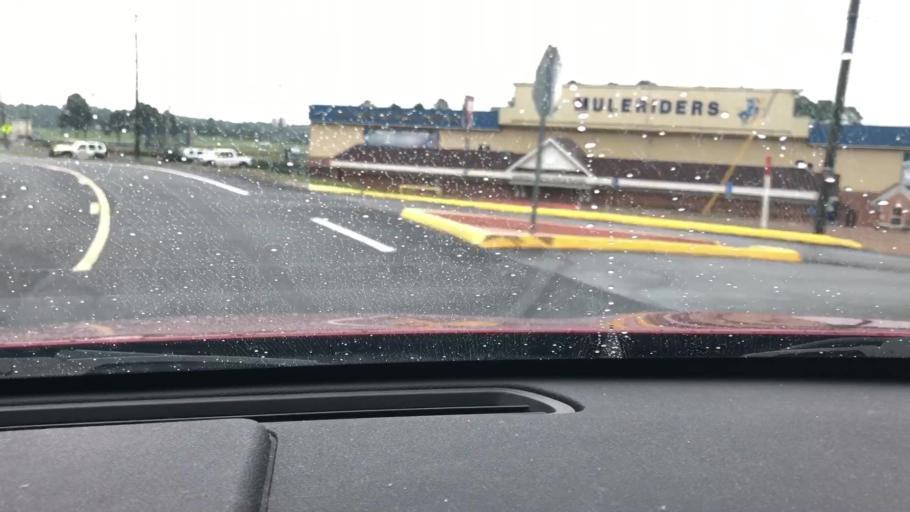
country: US
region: Arkansas
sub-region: Columbia County
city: Magnolia
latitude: 33.2944
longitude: -93.2361
